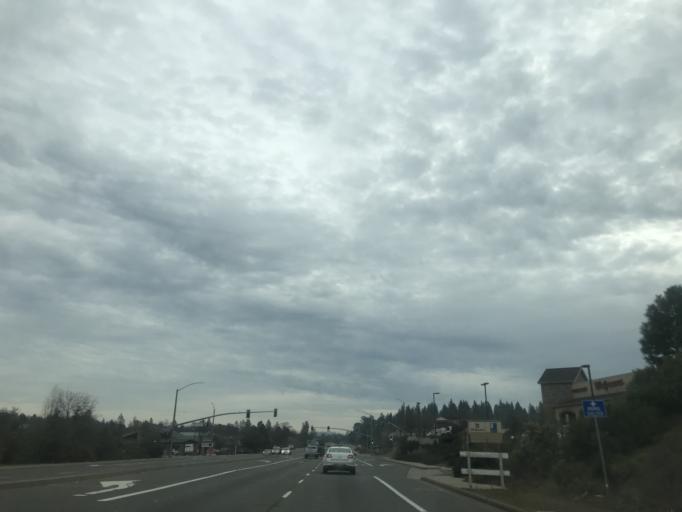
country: US
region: California
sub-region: El Dorado County
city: Diamond Springs
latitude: 38.7074
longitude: -120.8319
